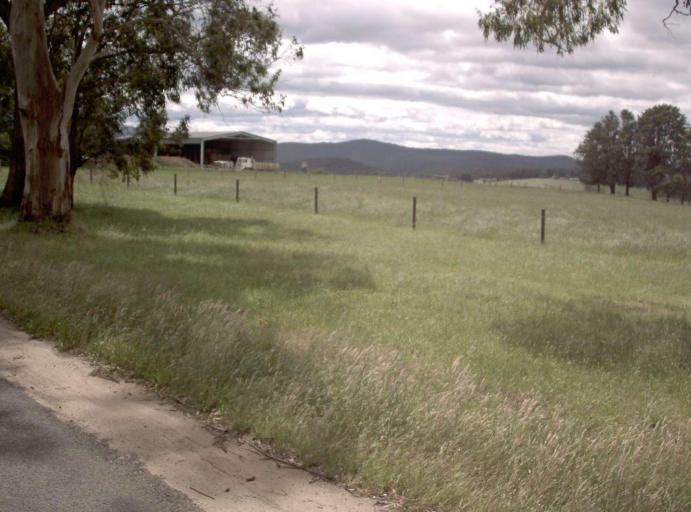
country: AU
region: Victoria
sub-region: Latrobe
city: Moe
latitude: -37.9987
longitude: 146.1453
